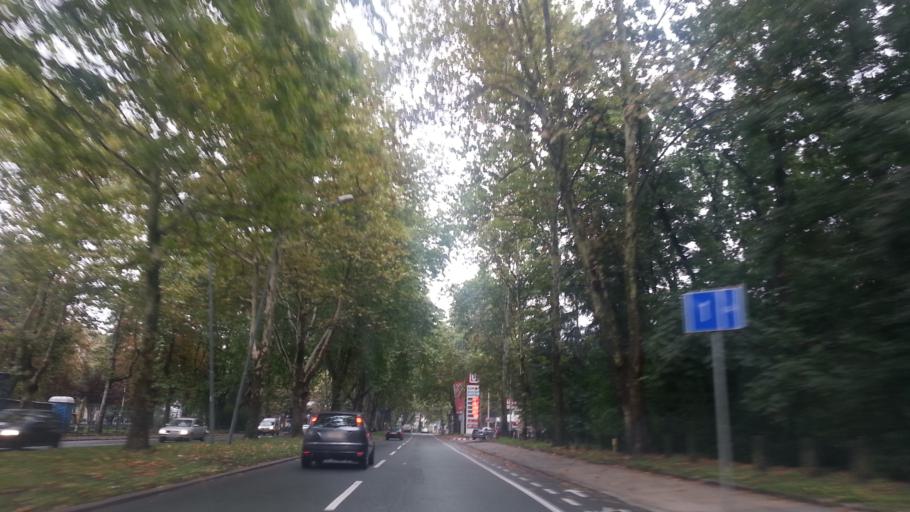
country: RS
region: Central Serbia
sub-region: Belgrade
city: Vozdovac
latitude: 44.7723
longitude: 20.4747
